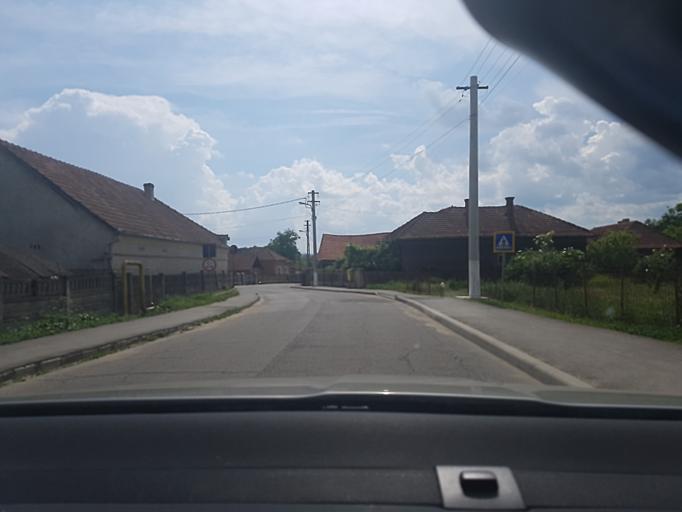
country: RO
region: Hunedoara
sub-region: Comuna Calan
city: Calan
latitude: 45.7286
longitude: 23.0213
